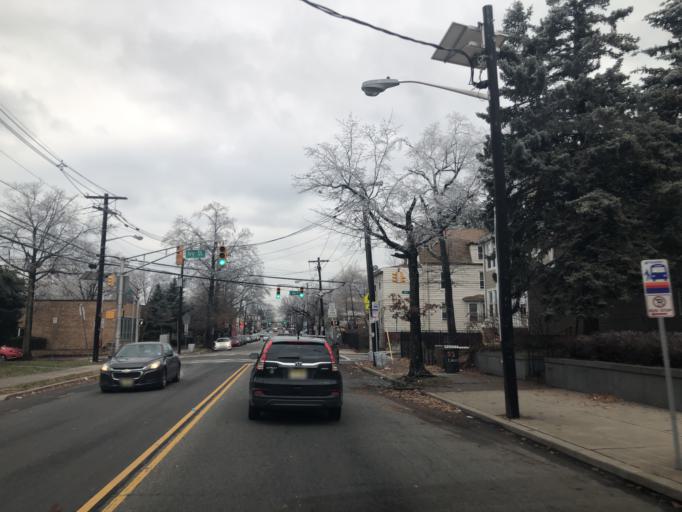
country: US
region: New Jersey
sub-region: Essex County
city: Irvington
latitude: 40.7371
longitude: -74.2363
